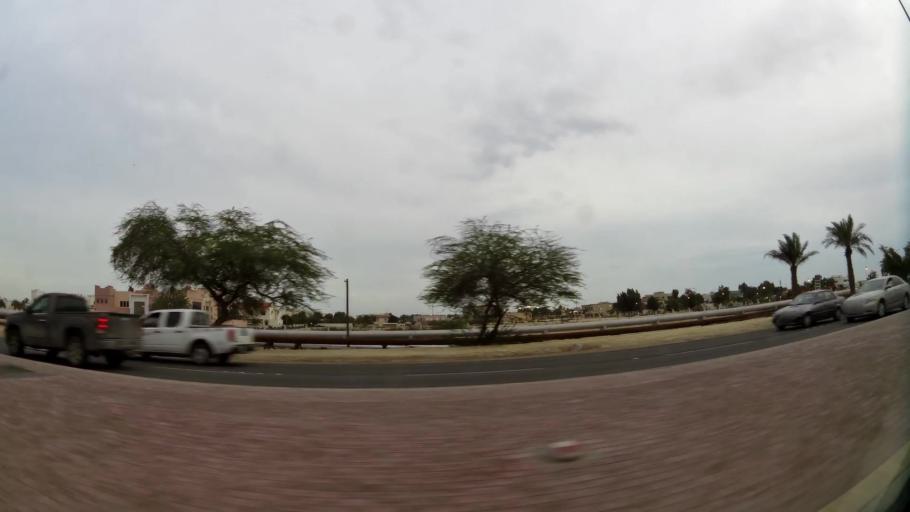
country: BH
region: Northern
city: Ar Rifa'
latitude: 26.1354
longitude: 50.5311
